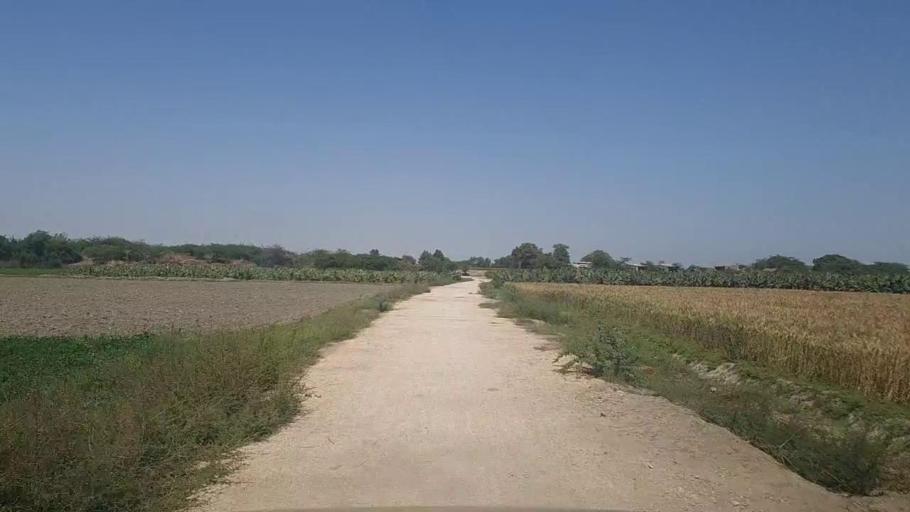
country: PK
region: Sindh
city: Thatta
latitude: 24.7890
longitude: 68.0147
